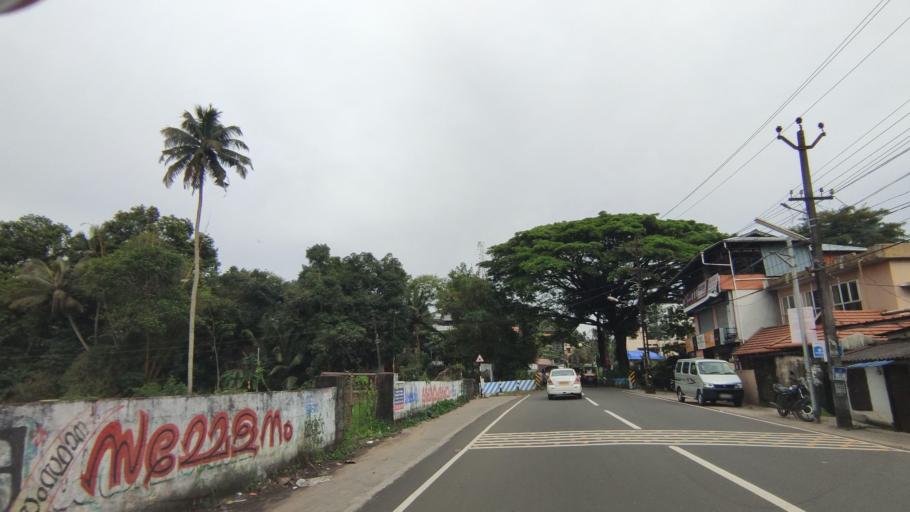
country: IN
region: Kerala
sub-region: Kottayam
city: Kottayam
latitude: 9.5959
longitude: 76.5127
